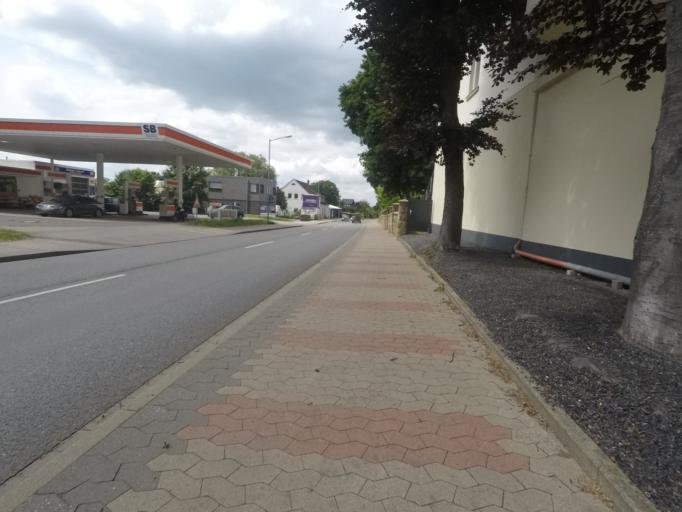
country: DE
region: North Rhine-Westphalia
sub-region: Regierungsbezirk Detmold
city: Hiddenhausen
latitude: 52.1826
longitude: 8.6063
